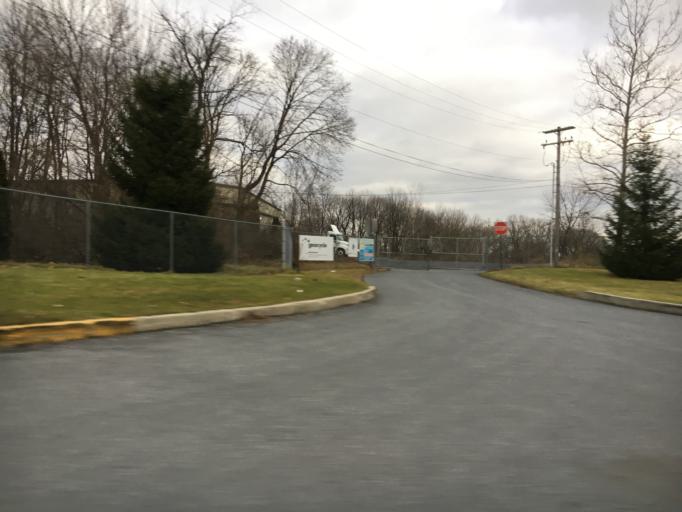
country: US
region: Pennsylvania
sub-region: Northampton County
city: Northampton
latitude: 40.6977
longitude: -75.4993
